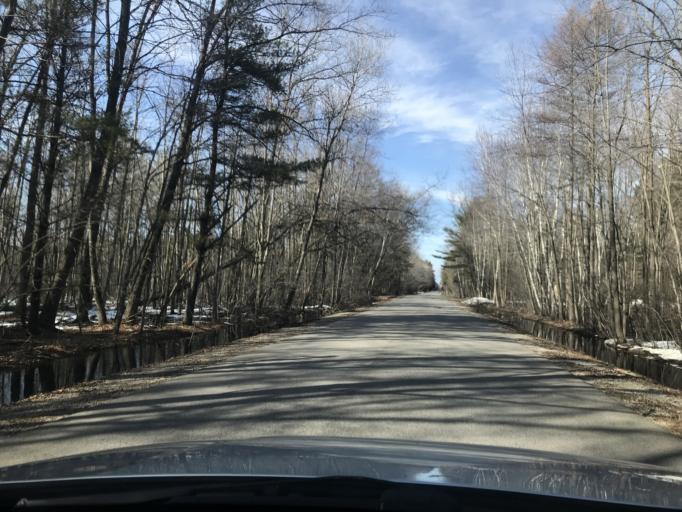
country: US
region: Wisconsin
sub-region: Marinette County
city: Marinette
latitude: 45.0248
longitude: -87.6674
